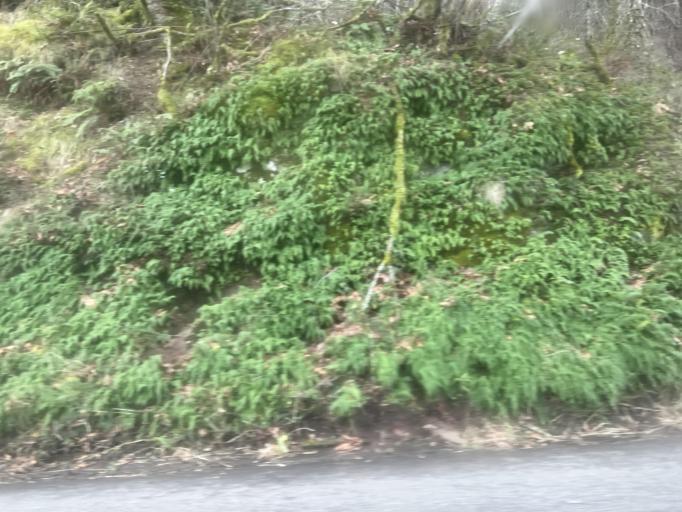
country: US
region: Washington
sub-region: Clark County
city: Washougal
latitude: 45.5413
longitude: -122.2110
